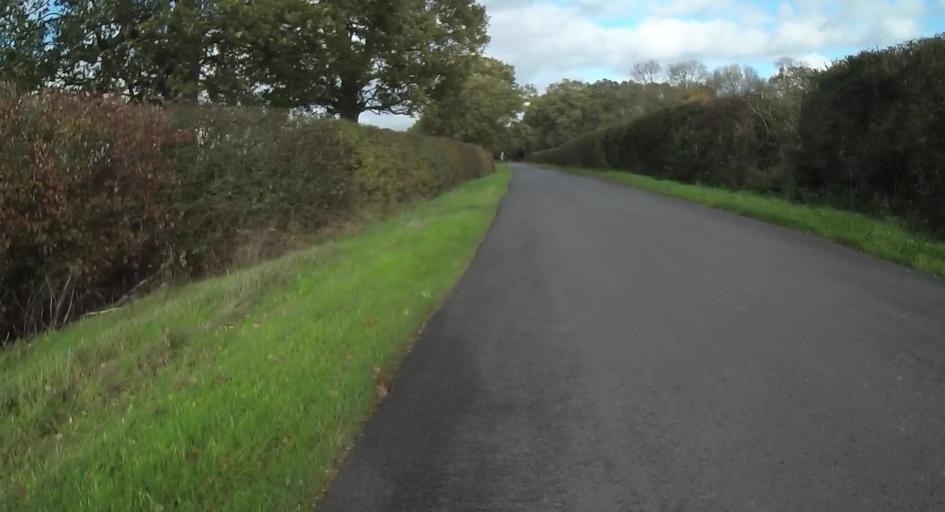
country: GB
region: England
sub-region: West Berkshire
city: Stratfield Mortimer
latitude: 51.3619
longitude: -1.0011
